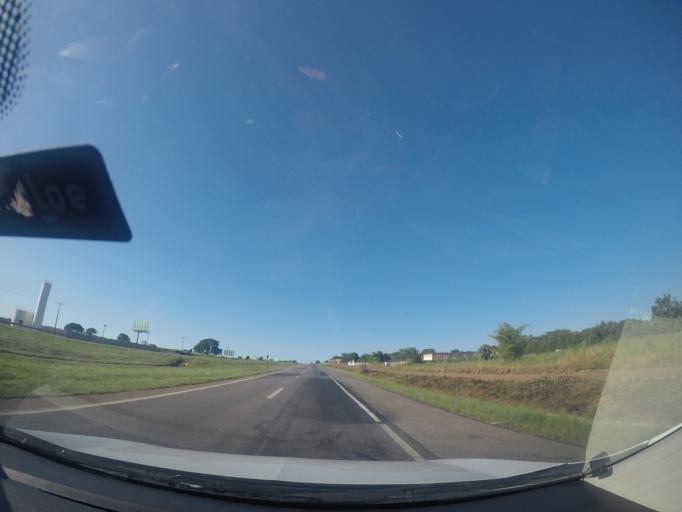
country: BR
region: Goias
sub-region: Aparecida De Goiania
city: Aparecida de Goiania
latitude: -16.8750
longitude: -49.2521
